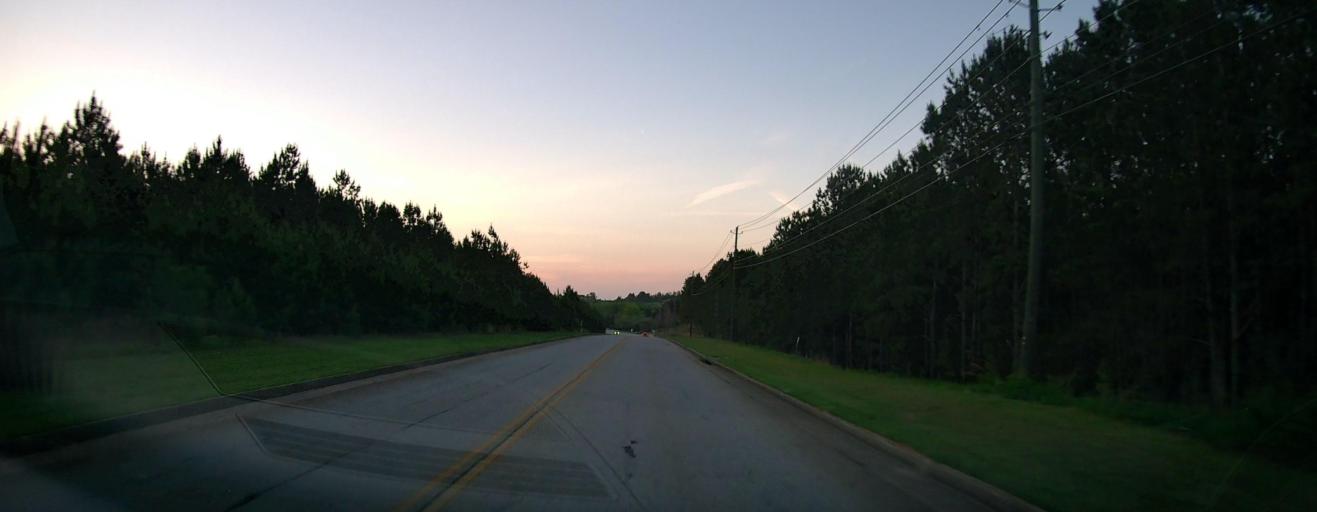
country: US
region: Georgia
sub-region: Henry County
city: Stockbridge
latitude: 33.4946
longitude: -84.2186
